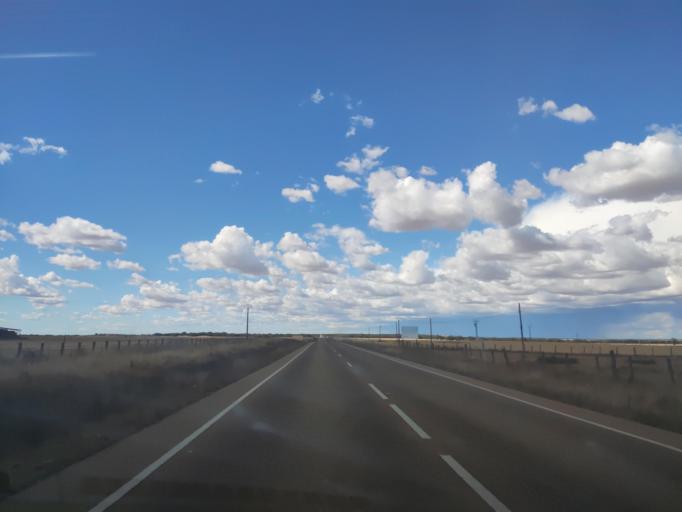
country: ES
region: Castille and Leon
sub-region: Provincia de Salamanca
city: La Fuente de San Esteban
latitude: 40.8084
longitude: -6.2584
